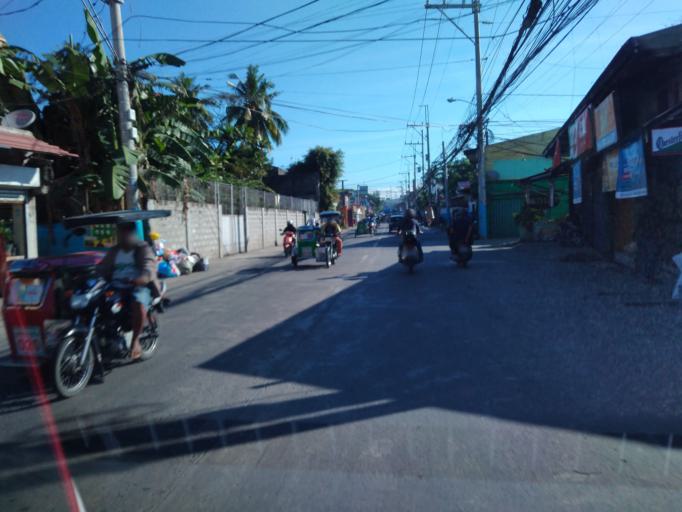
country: PH
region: Central Luzon
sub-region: Province of Bulacan
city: Meycauayan
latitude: 14.7389
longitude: 120.9656
